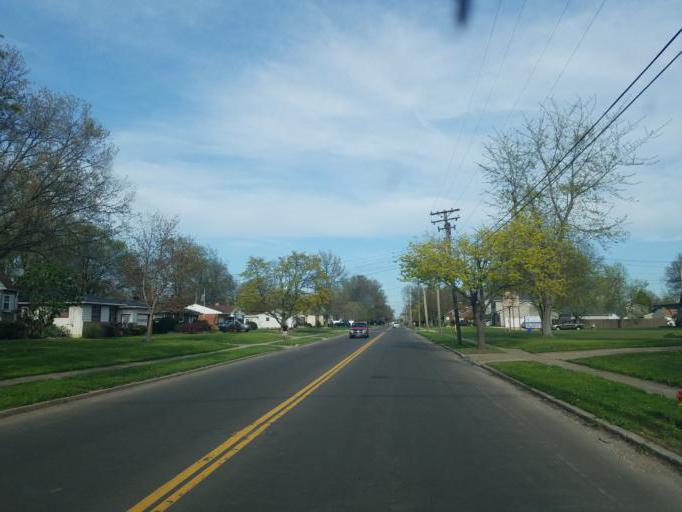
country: US
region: Ohio
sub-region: Ashtabula County
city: Ashtabula
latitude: 41.8925
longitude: -80.8151
